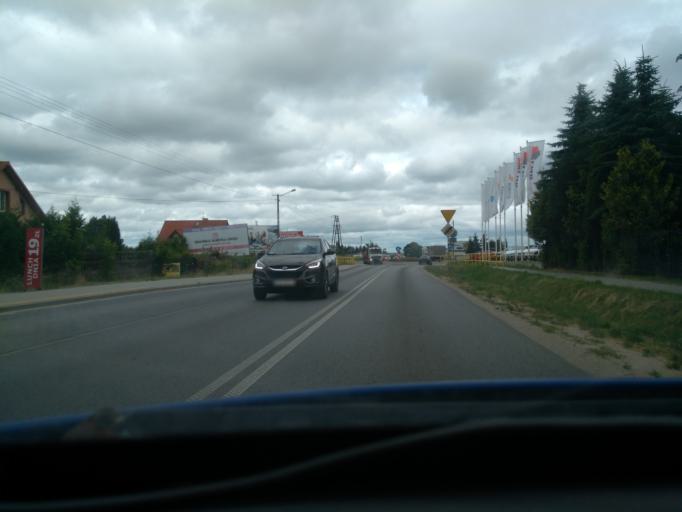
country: PL
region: Pomeranian Voivodeship
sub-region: Powiat kartuski
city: Banino
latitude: 54.3933
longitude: 18.3821
